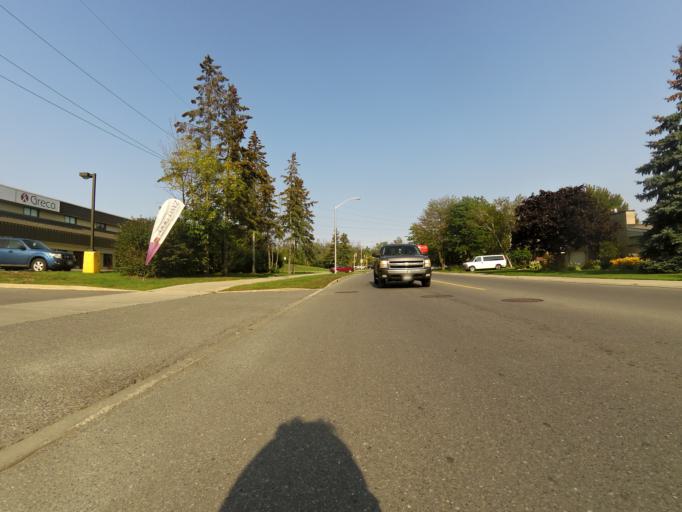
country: CA
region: Ontario
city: Bells Corners
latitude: 45.3002
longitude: -75.8764
